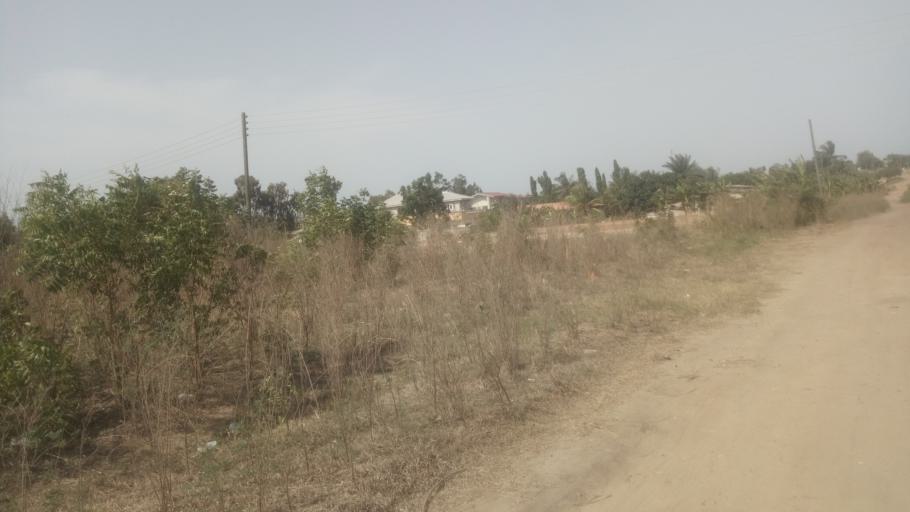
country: GH
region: Central
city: Winneba
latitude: 5.3773
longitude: -0.6506
